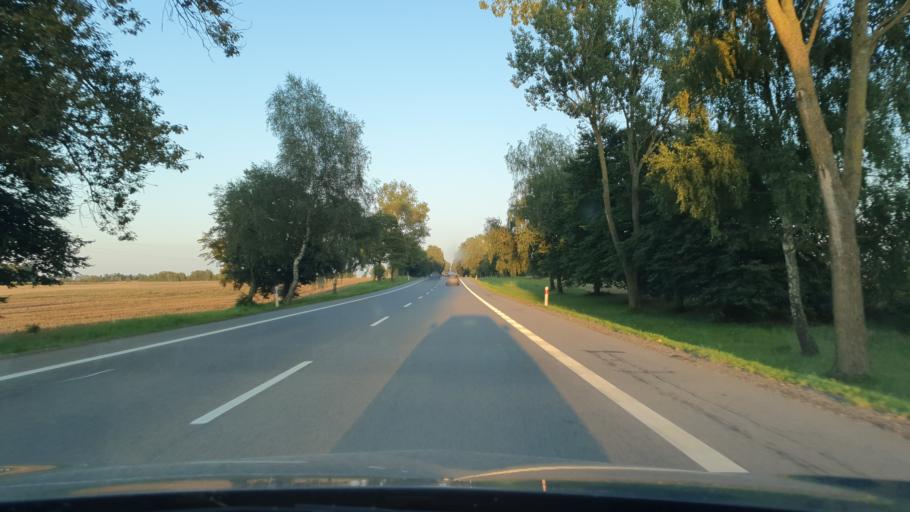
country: PL
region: Pomeranian Voivodeship
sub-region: Powiat slupski
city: Potegowo
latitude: 54.4770
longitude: 17.5049
